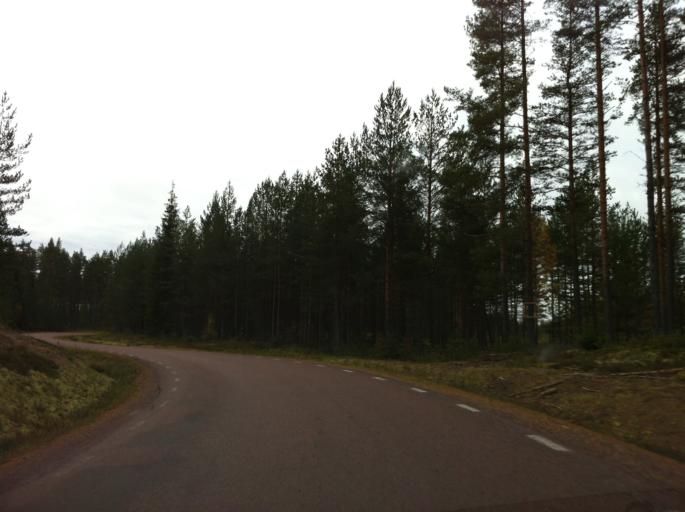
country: SE
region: Dalarna
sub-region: Mora Kommun
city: Mora
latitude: 61.1041
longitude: 14.4526
